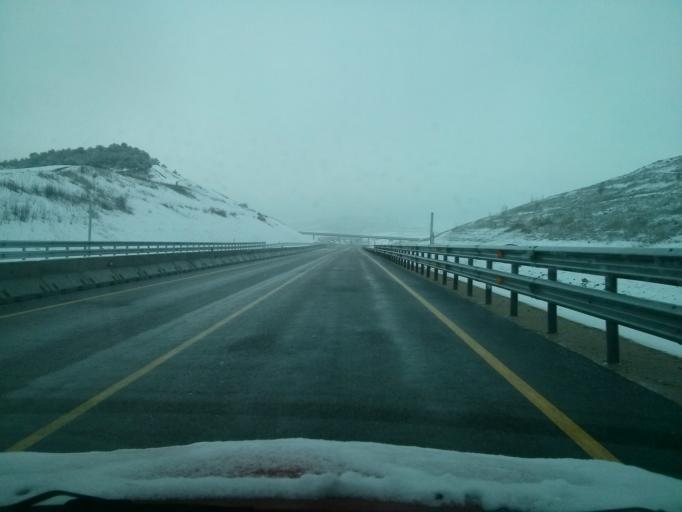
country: ES
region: Castille and Leon
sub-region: Provincia de Burgos
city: Burgos
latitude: 42.3843
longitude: -3.6787
